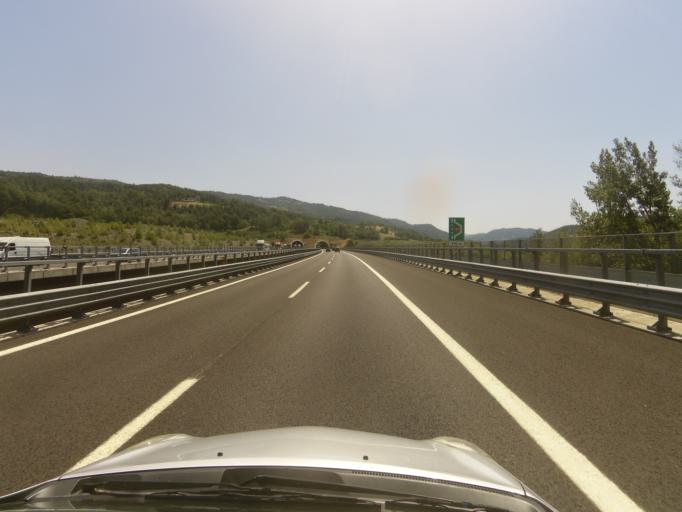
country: IT
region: Emilia-Romagna
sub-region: Provincia di Bologna
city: Grizzana
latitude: 44.2622
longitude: 11.1879
